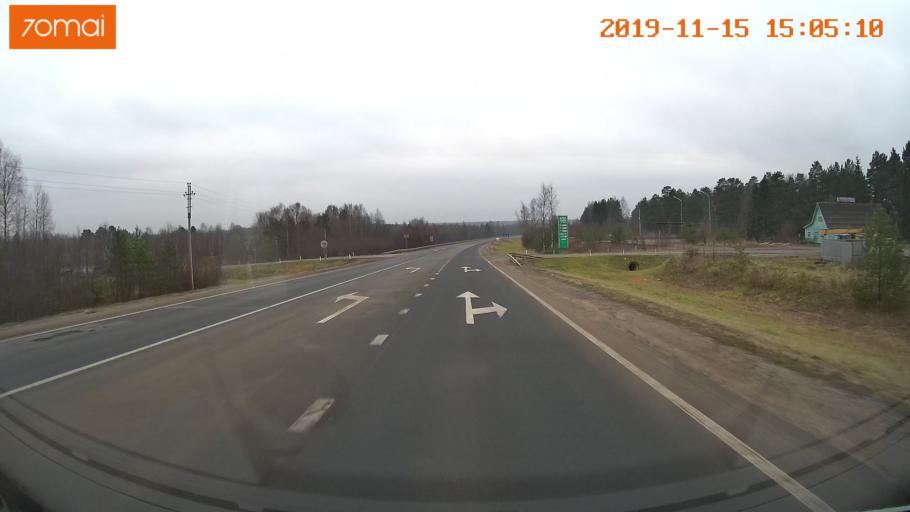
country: RU
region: Jaroslavl
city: Prechistoye
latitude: 58.4077
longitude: 40.3251
